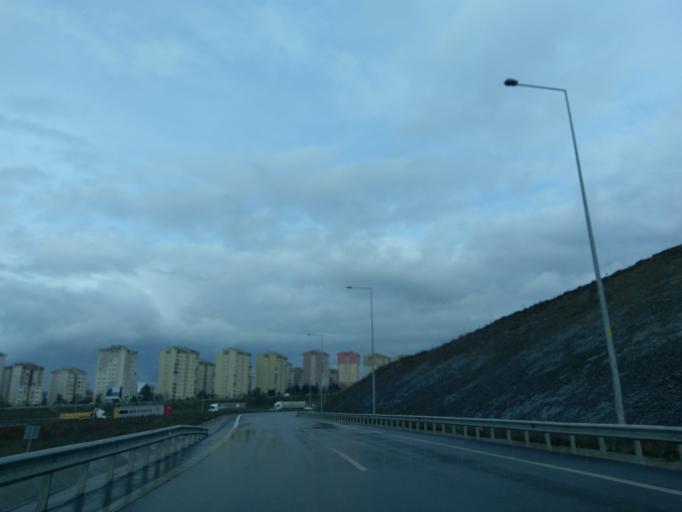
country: TR
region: Istanbul
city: Basaksehir
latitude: 41.0841
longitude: 28.8150
